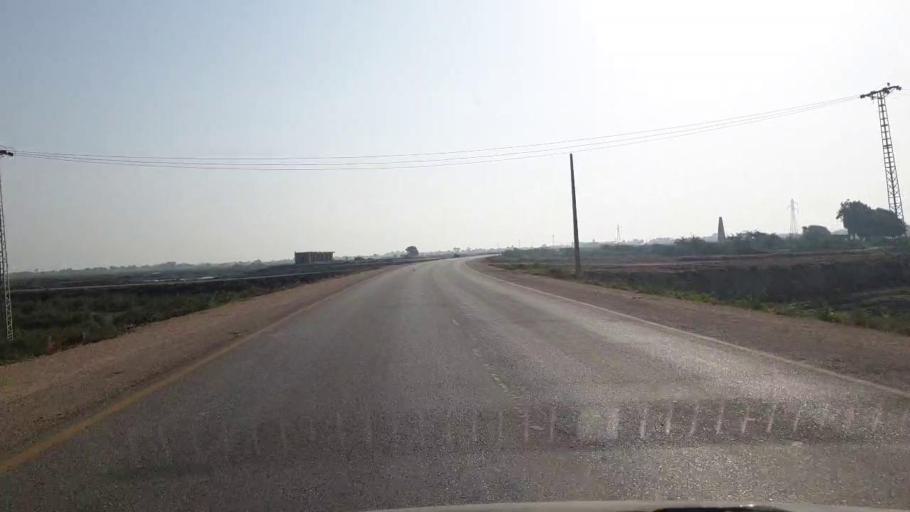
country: PK
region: Sindh
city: Badin
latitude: 24.6810
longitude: 68.8381
